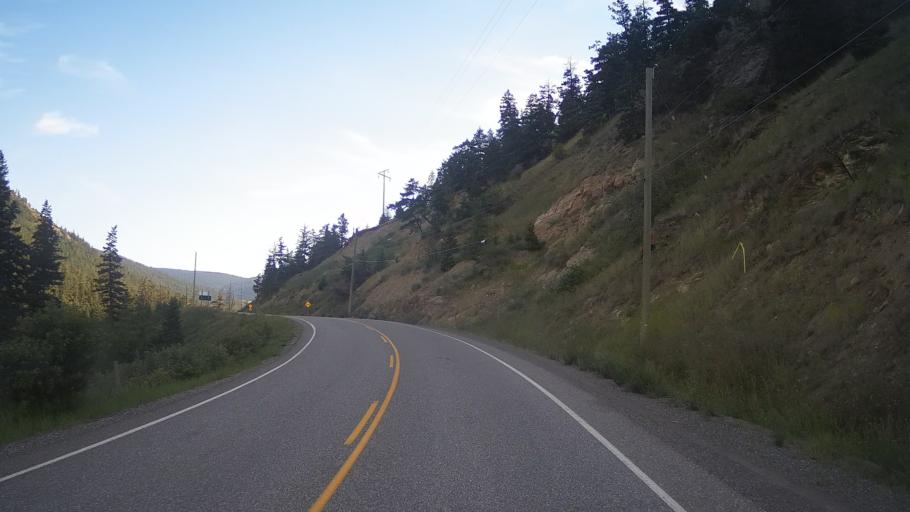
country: CA
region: British Columbia
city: Cache Creek
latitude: 50.8662
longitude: -121.5260
